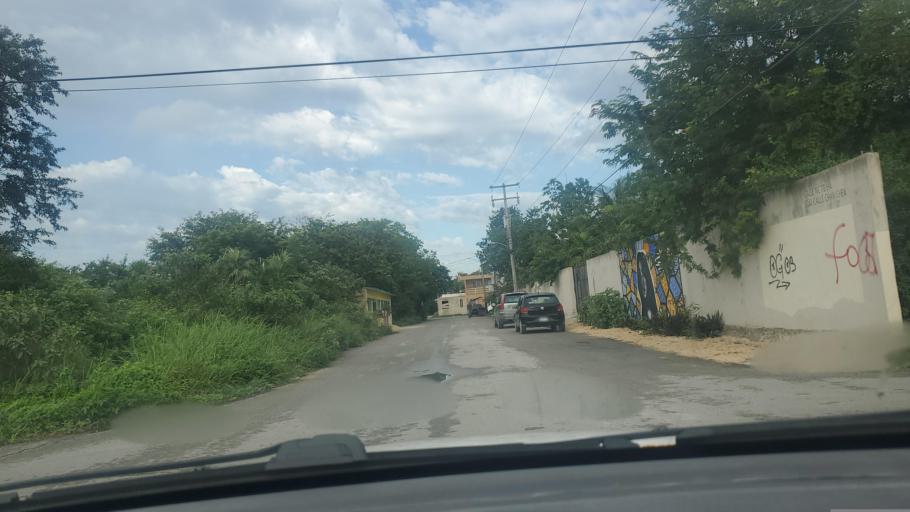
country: MX
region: Quintana Roo
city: Tulum
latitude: 20.2123
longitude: -87.4701
